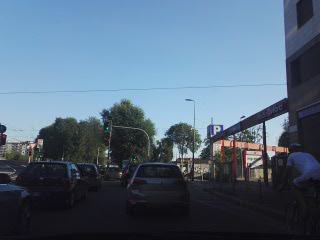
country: IT
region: Lombardy
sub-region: Citta metropolitana di Milano
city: Milano
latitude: 45.4504
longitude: 9.1554
